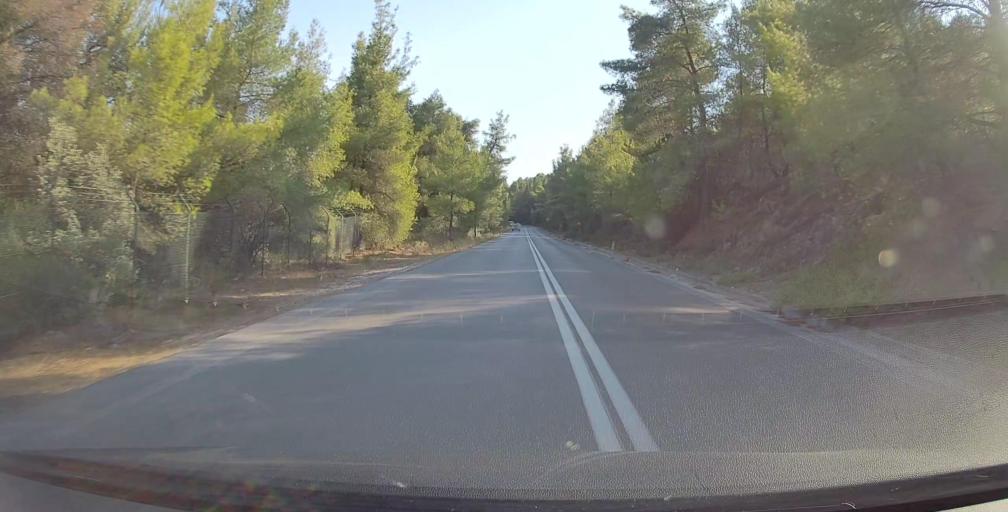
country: GR
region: Central Macedonia
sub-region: Nomos Chalkidikis
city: Neos Marmaras
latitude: 40.0682
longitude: 23.8043
